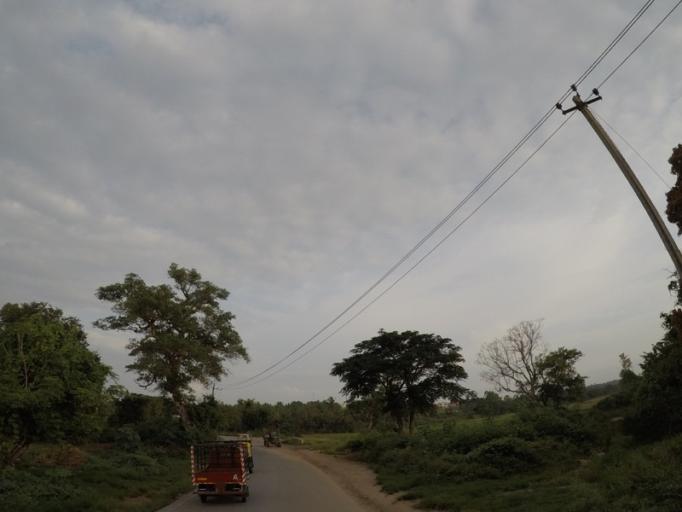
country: IN
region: Karnataka
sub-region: Hassan
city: Belur
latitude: 13.1771
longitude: 75.8712
